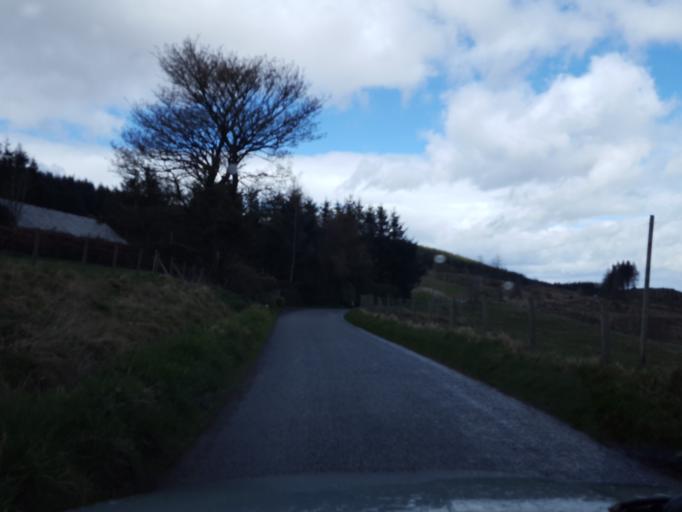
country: GB
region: Scotland
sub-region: Perth and Kinross
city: Auchterarder
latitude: 56.2680
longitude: -3.5839
